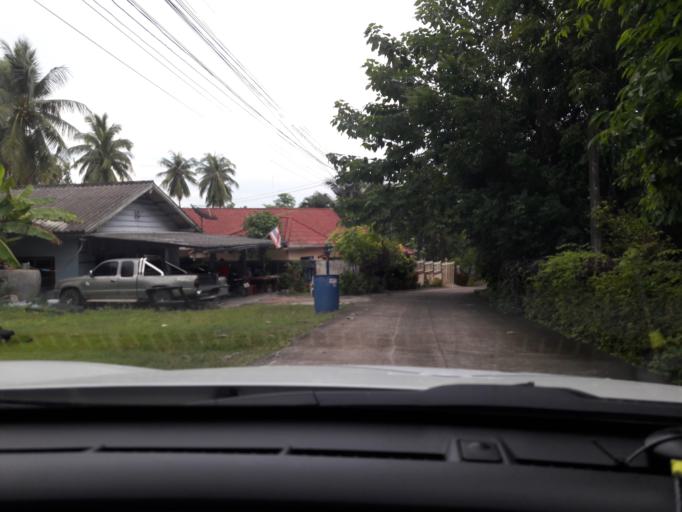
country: TH
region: Nakhon Sawan
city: Tak Fa
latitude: 15.3513
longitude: 100.4992
